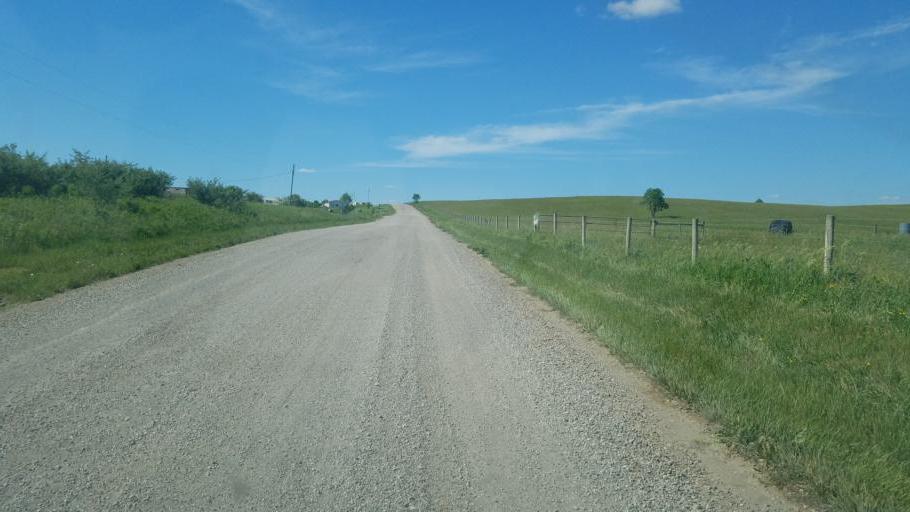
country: US
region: Ohio
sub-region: Tuscarawas County
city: Newcomerstown
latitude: 40.2388
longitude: -81.6720
